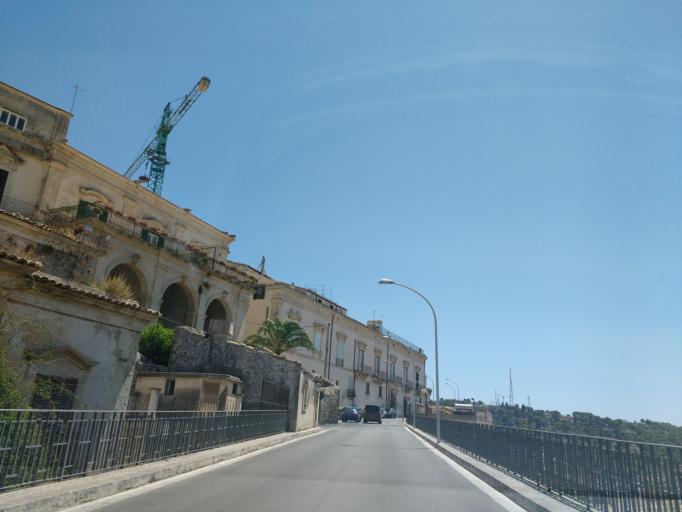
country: IT
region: Sicily
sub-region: Ragusa
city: Modica
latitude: 36.8632
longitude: 14.7614
